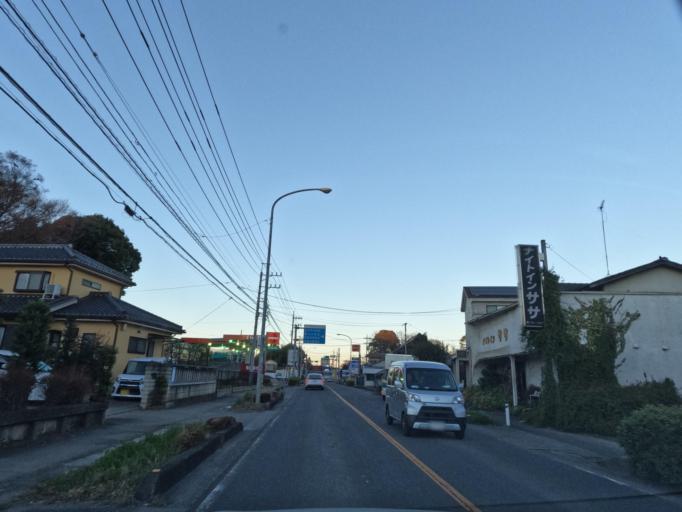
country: JP
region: Saitama
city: Iwatsuki
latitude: 35.9820
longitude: 139.6990
